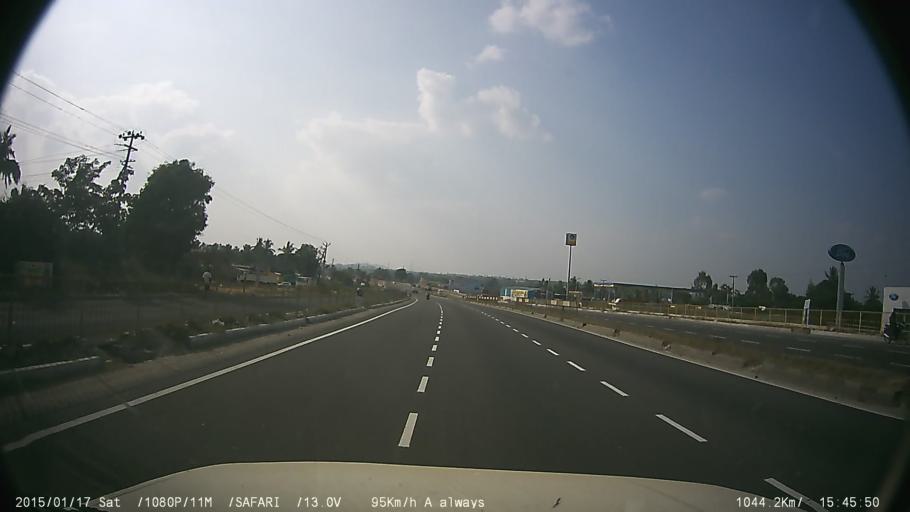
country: IN
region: Tamil Nadu
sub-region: Krishnagiri
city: Hosur
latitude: 12.7106
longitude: 77.8971
